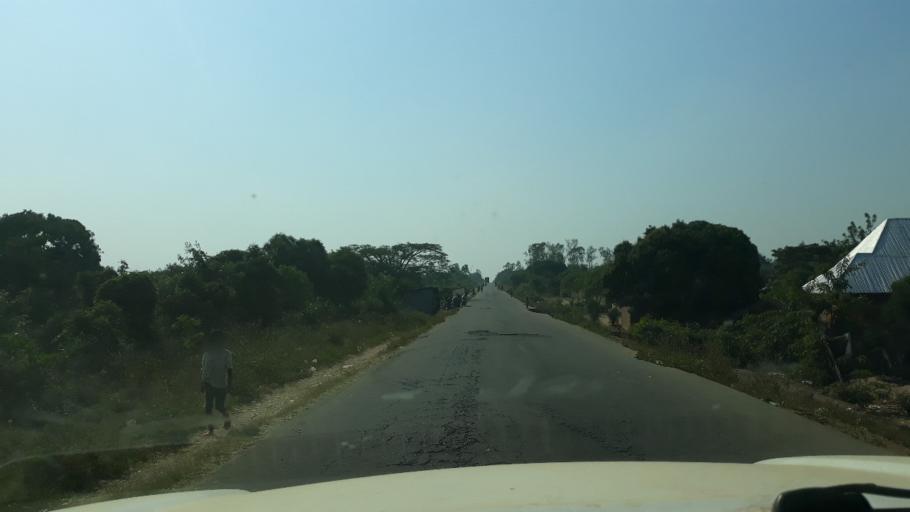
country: BI
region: Cibitoke
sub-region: Commune of Buganda
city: Buganda
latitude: -3.0713
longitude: 29.1222
